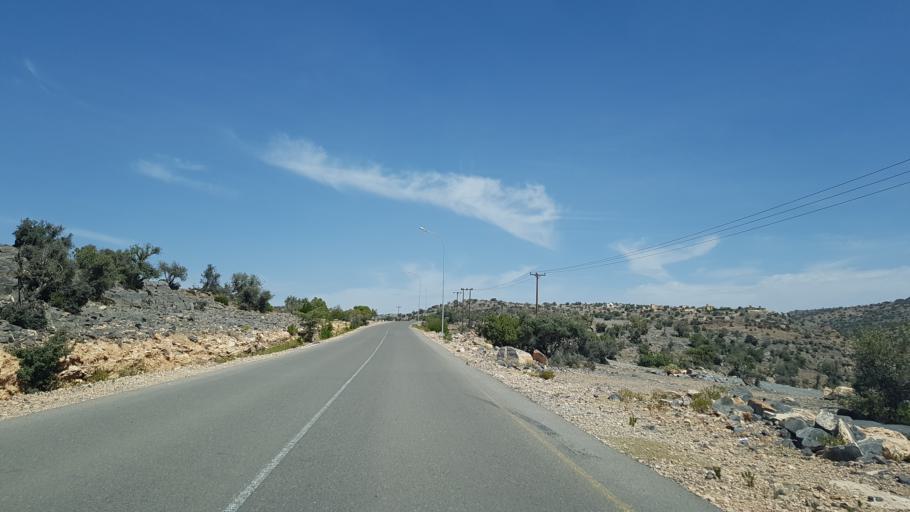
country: OM
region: Al Batinah
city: Bayt al `Awabi
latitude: 23.1382
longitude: 57.5783
